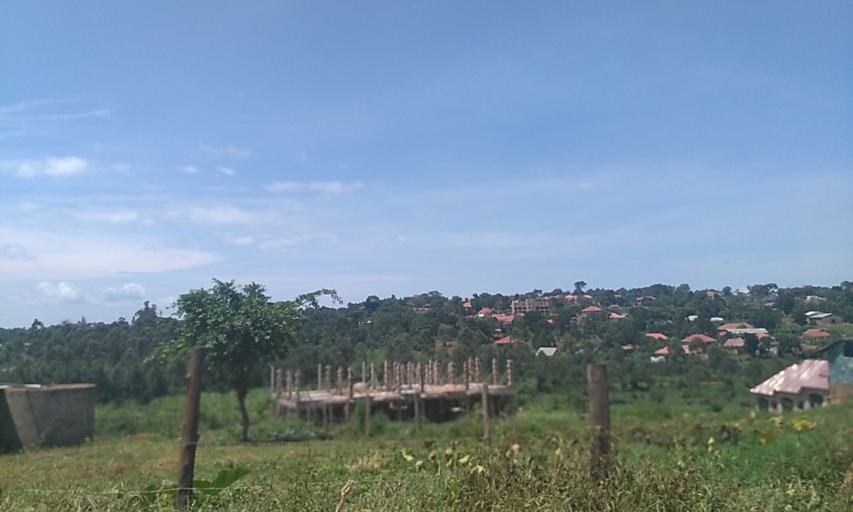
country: UG
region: Central Region
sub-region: Wakiso District
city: Wakiso
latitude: 0.4072
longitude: 32.4719
